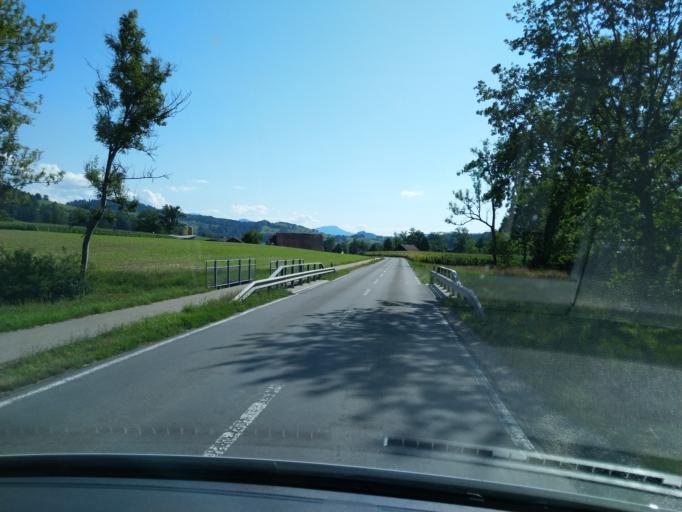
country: CH
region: Lucerne
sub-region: Sursee District
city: Ruswil
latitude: 47.0767
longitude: 8.1086
